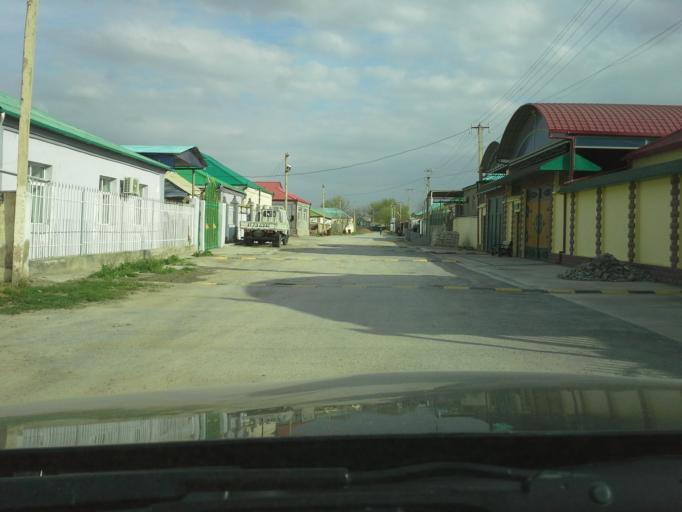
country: TM
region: Ahal
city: Abadan
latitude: 37.9661
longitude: 58.2125
